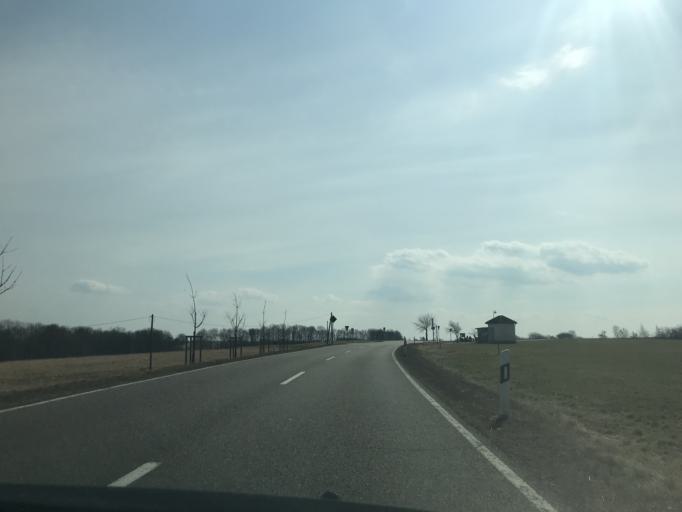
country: DE
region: Saxony
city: Seelitz
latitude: 51.0206
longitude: 12.8116
